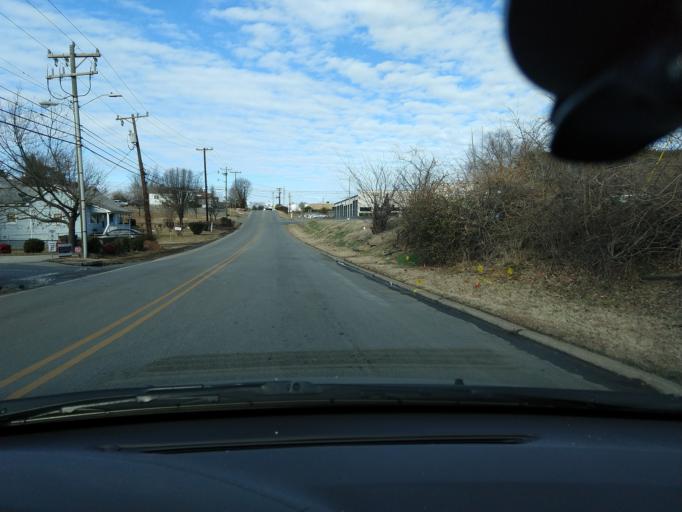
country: US
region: North Carolina
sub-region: Guilford County
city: Greensboro
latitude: 36.0619
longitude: -79.8706
